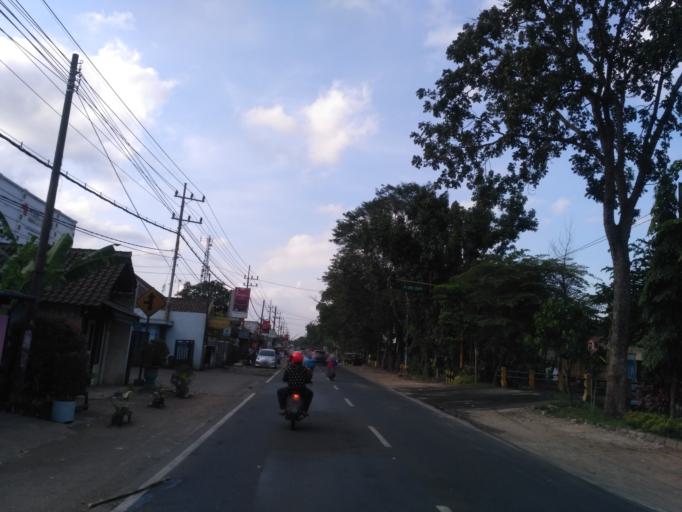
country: ID
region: East Java
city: Pakisaji
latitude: -8.0570
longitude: 112.6031
